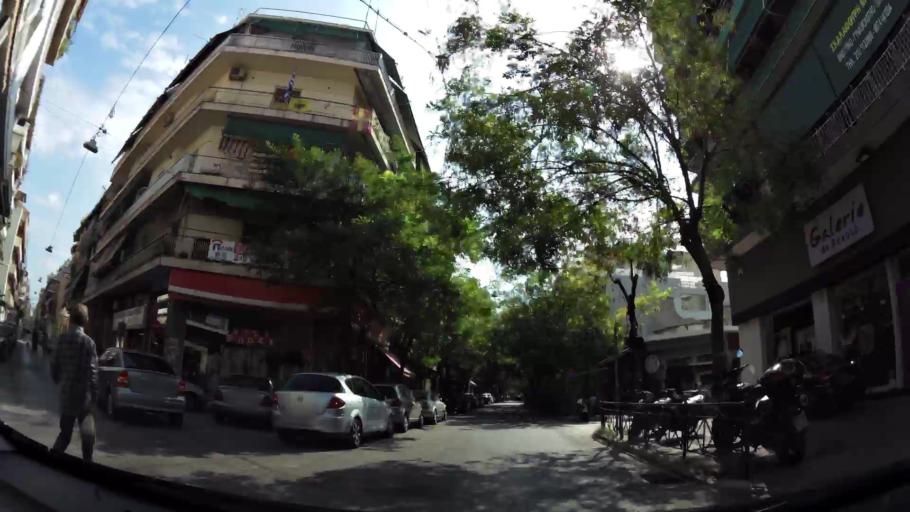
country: GR
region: Attica
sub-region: Nomarchia Athinas
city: Kipseli
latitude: 38.0042
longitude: 23.7183
